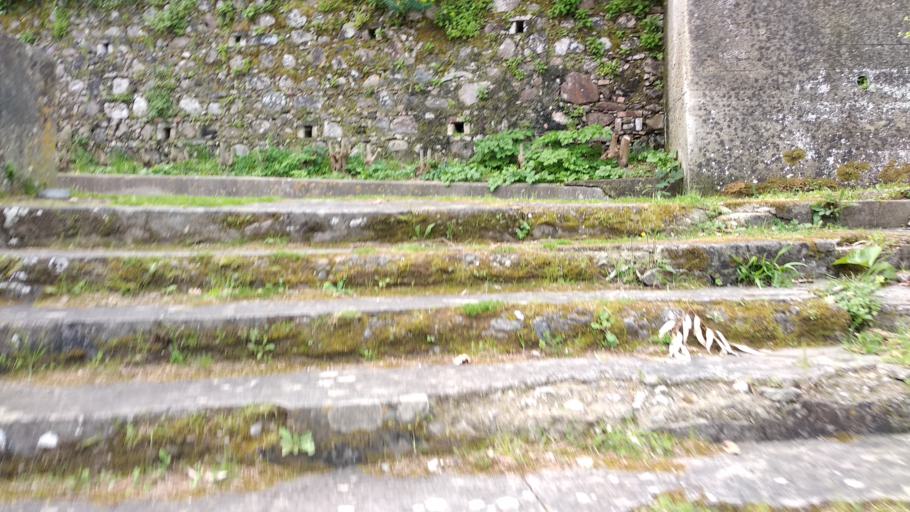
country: IT
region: Sicily
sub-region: Messina
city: Villafranca Tirrena
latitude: 38.2214
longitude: 15.4531
